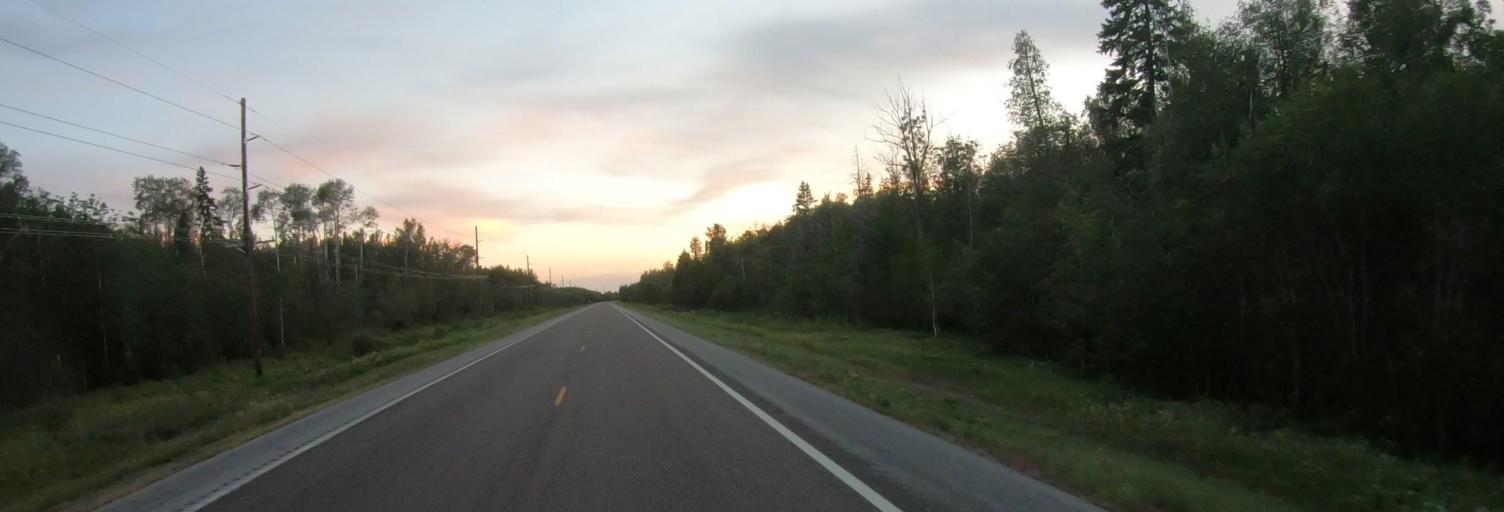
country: US
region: Minnesota
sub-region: Saint Louis County
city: Parkville
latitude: 47.8495
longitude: -92.5039
